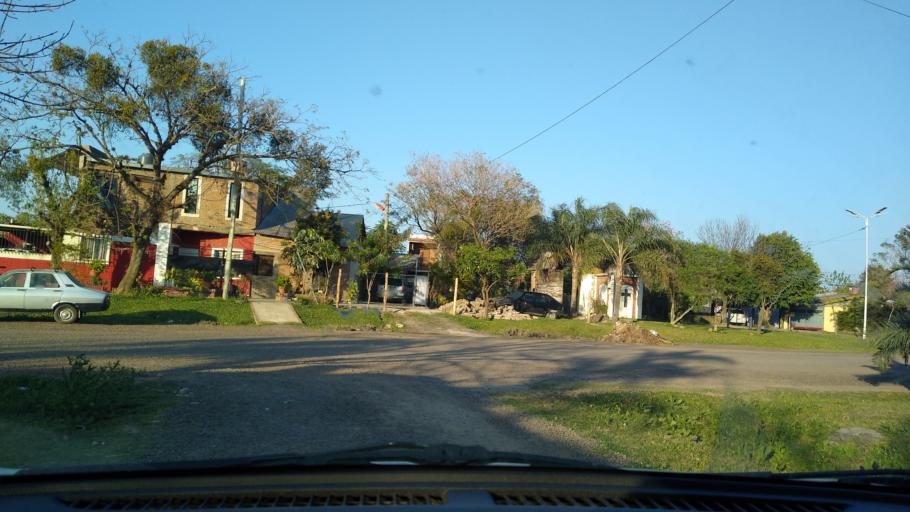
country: AR
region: Chaco
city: Barranqueras
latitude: -27.4746
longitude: -58.9524
